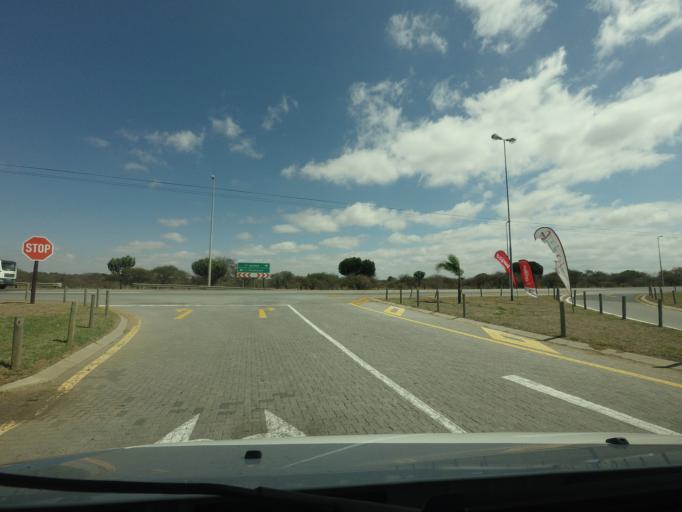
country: ZA
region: Limpopo
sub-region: Vhembe District Municipality
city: Louis Trichardt
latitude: -23.3622
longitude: 29.7793
